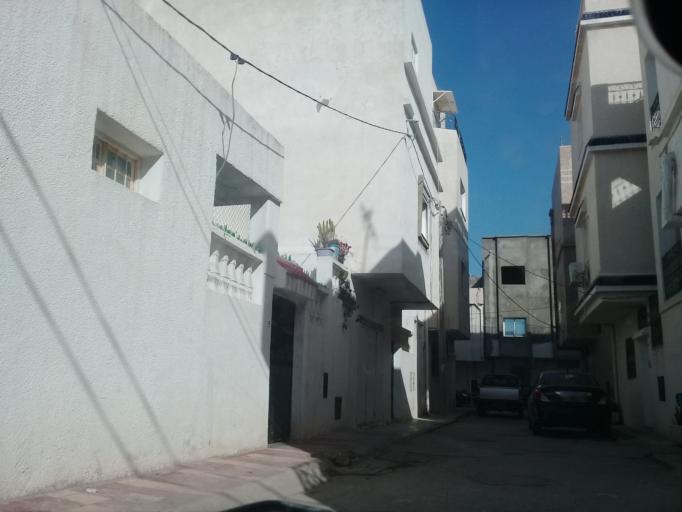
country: TN
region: Ariana
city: Ariana
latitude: 36.8314
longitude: 10.1928
